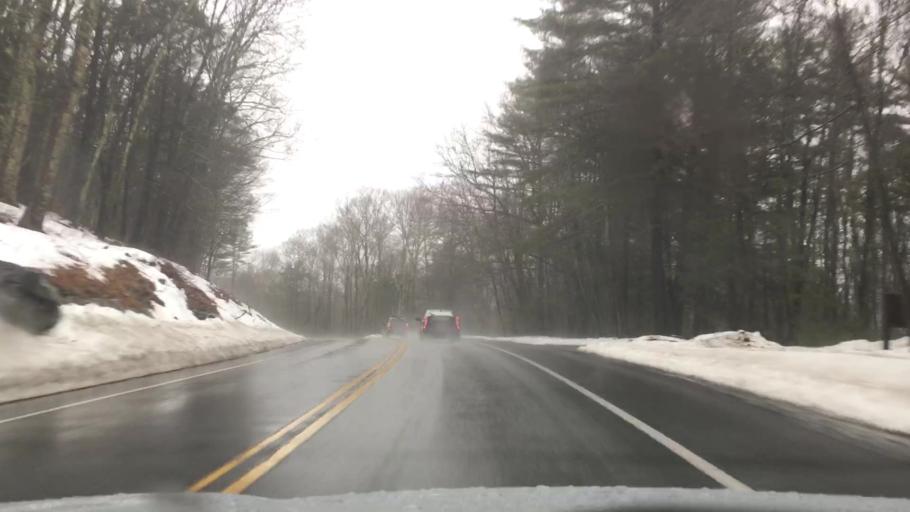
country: US
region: Massachusetts
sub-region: Franklin County
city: Shutesbury
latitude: 42.4727
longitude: -72.3513
